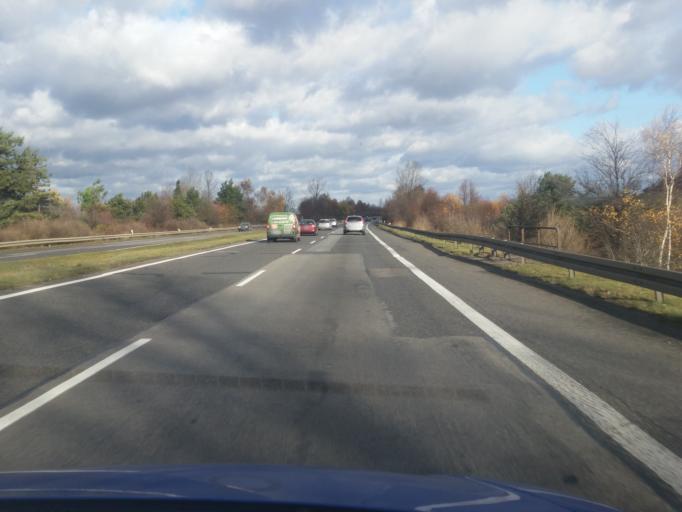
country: PL
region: Silesian Voivodeship
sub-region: Powiat czestochowski
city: Redziny
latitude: 50.8645
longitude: 19.1548
